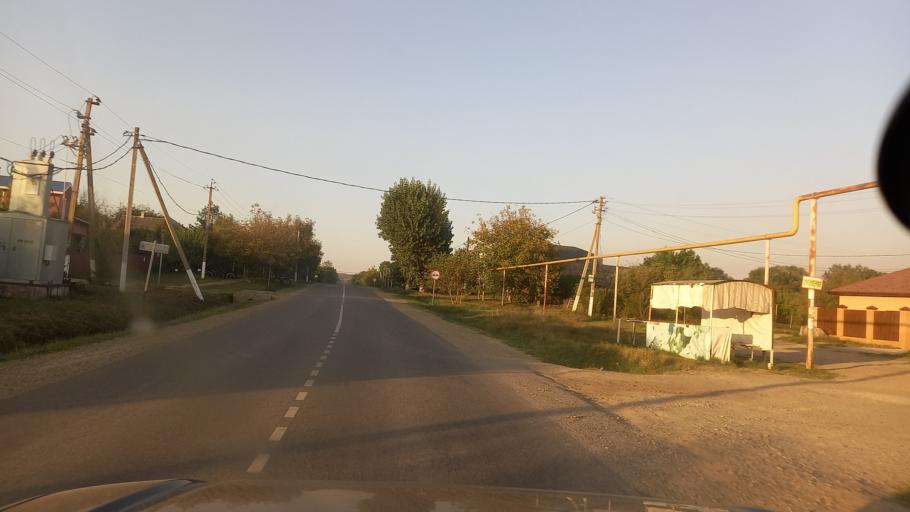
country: RU
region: Krasnodarskiy
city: Smolenskaya
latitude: 44.7696
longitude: 38.7822
